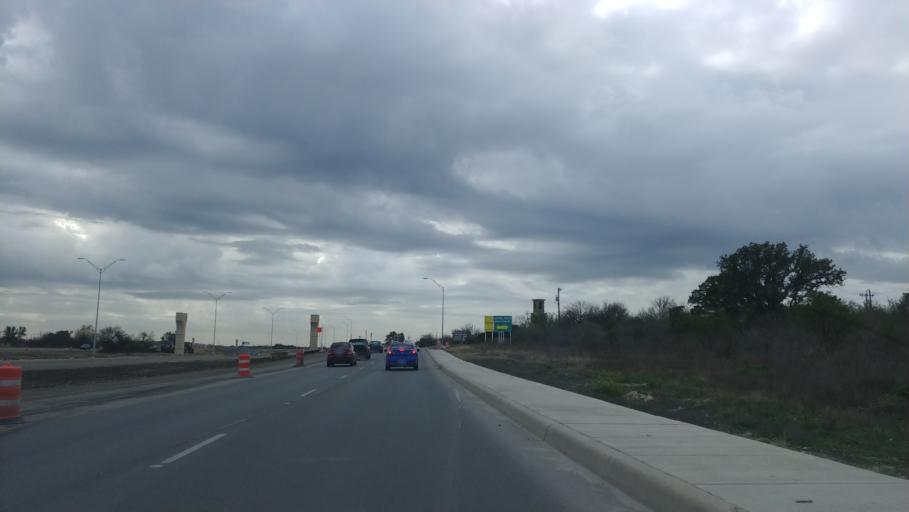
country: US
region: Texas
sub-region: Bexar County
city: Lackland Air Force Base
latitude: 29.4125
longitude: -98.7103
